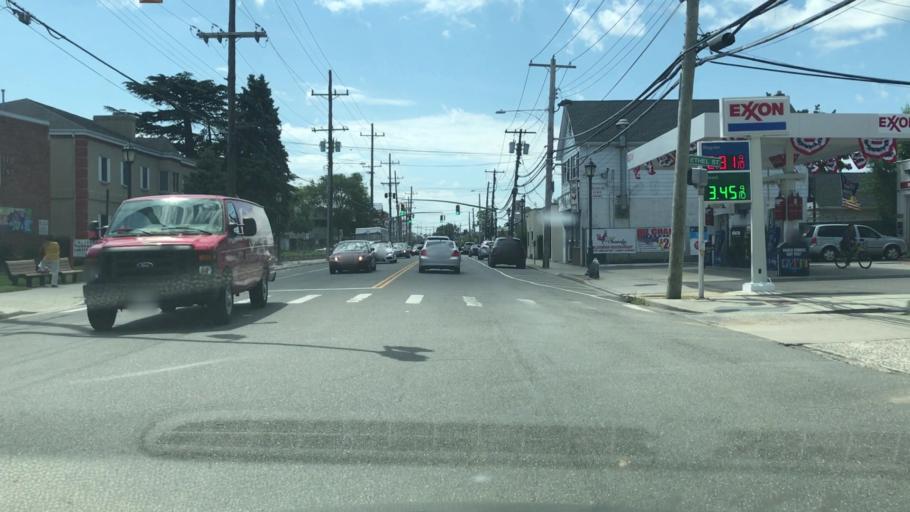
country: US
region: New York
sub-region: Nassau County
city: Valley Stream
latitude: 40.6737
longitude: -73.7094
